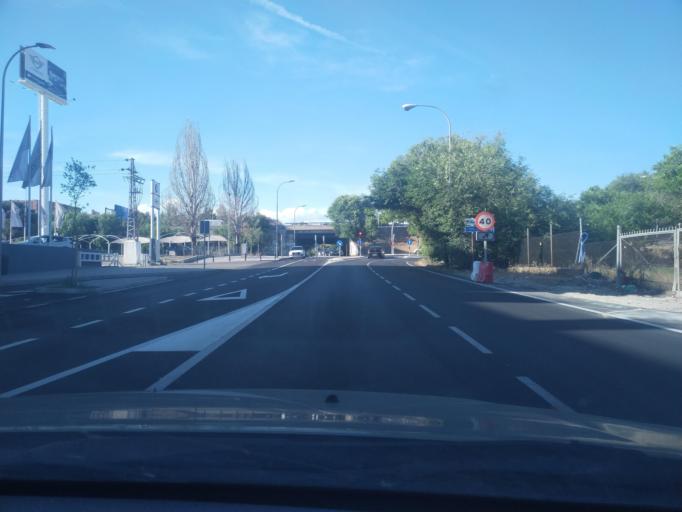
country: ES
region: Madrid
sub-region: Provincia de Madrid
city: Vicalvaro
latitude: 40.3896
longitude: -3.6224
